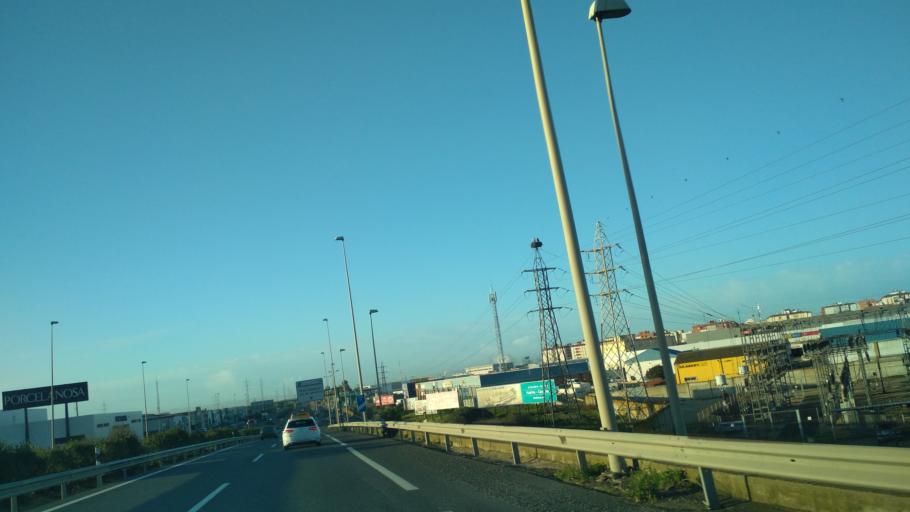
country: ES
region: Andalusia
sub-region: Provincia de Huelva
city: Huelva
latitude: 37.2680
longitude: -6.9179
